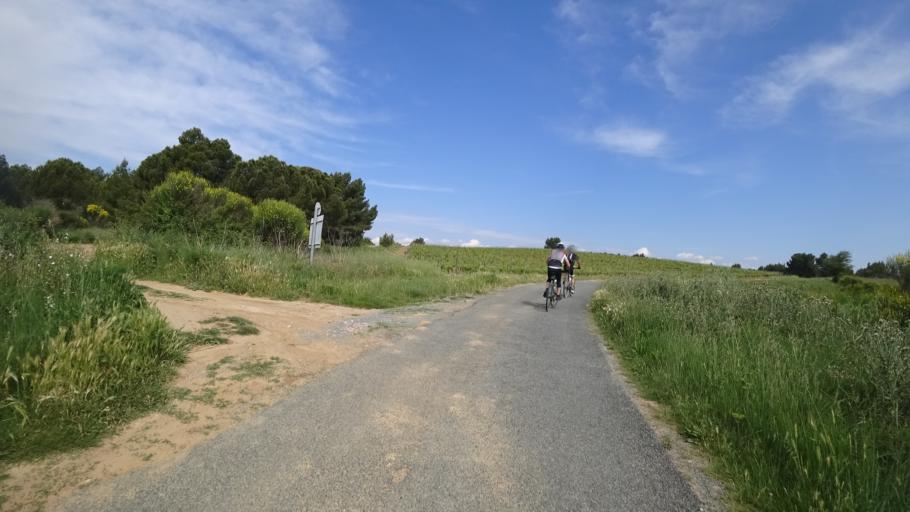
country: FR
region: Languedoc-Roussillon
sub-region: Departement de l'Aude
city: Canet
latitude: 43.2576
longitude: 2.8056
